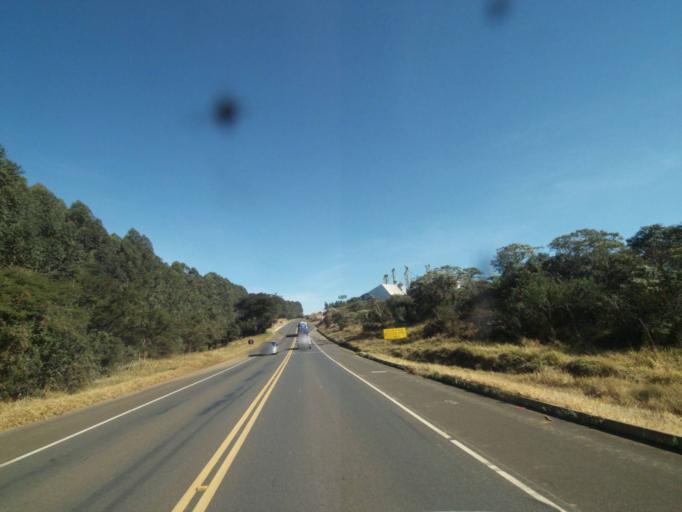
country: BR
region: Parana
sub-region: Tibagi
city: Tibagi
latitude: -24.5191
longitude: -50.4369
